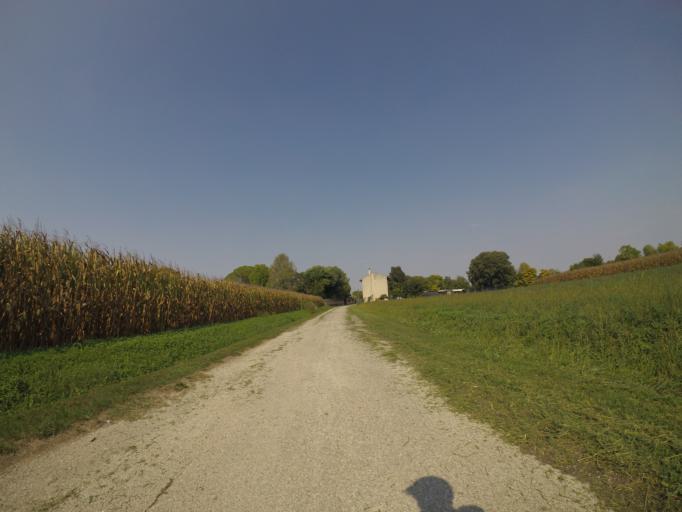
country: IT
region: Friuli Venezia Giulia
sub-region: Provincia di Udine
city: Camino al Tagliamento
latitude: 45.9149
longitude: 12.9287
